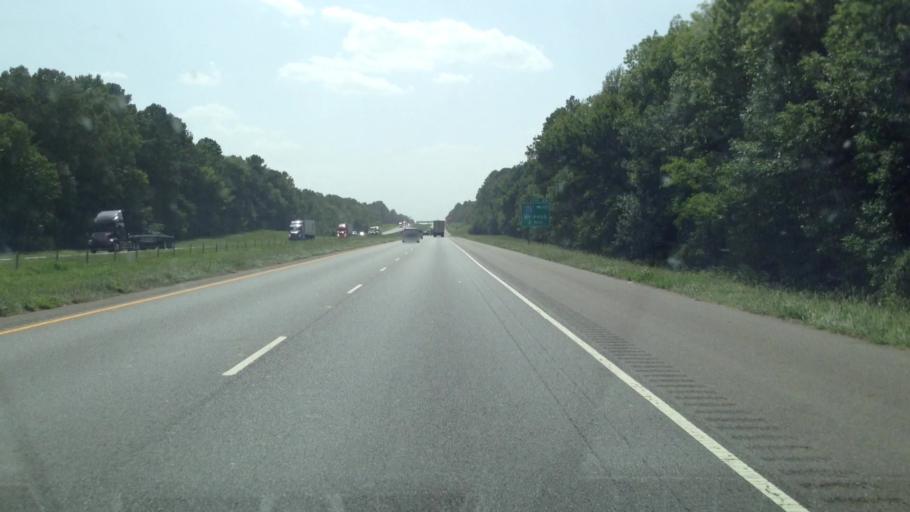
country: US
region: Louisiana
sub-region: Bossier Parish
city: Eastwood
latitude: 32.5421
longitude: -93.5857
